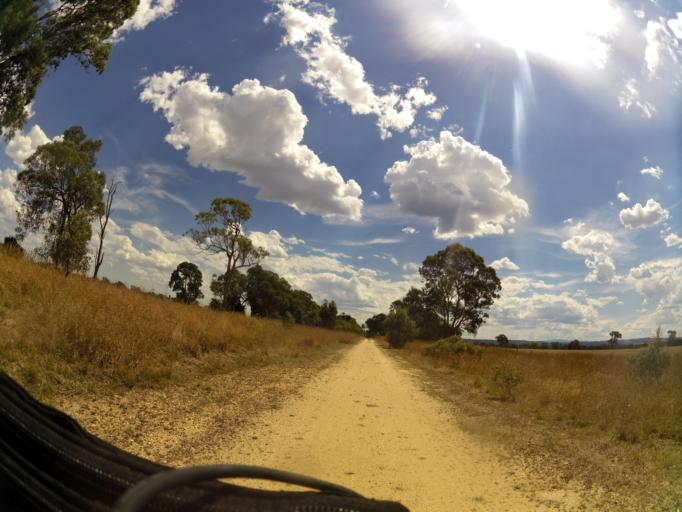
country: AU
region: Victoria
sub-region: Wellington
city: Heyfield
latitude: -37.9808
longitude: 146.7385
